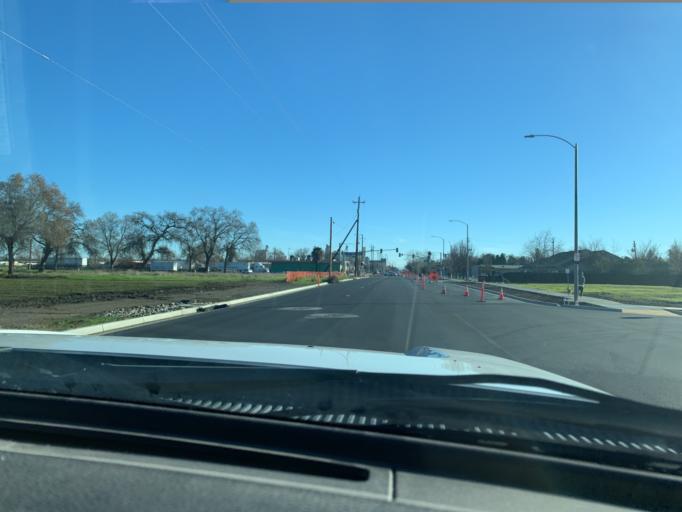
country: US
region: California
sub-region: Yolo County
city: Woodland
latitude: 38.6919
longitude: -121.7767
